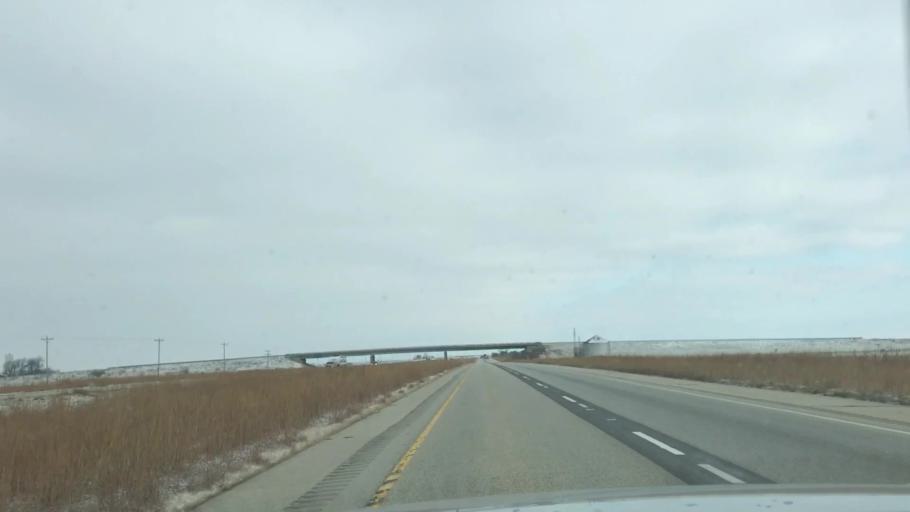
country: US
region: Illinois
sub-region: Sangamon County
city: Divernon
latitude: 39.4768
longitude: -89.6446
